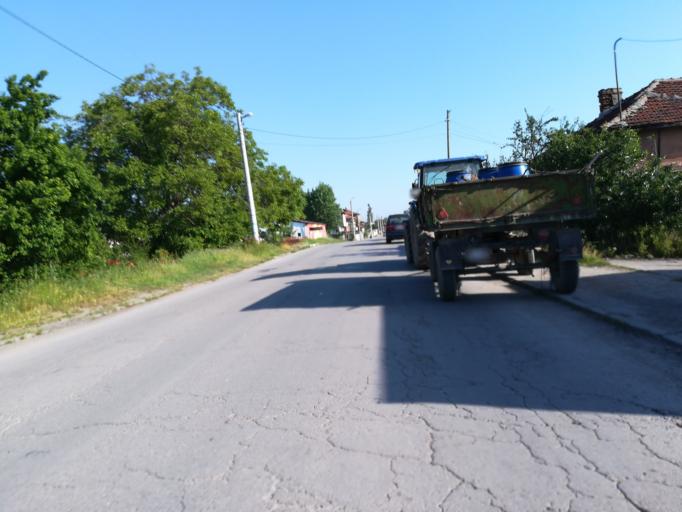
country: BG
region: Stara Zagora
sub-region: Obshtina Chirpan
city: Chirpan
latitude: 42.1049
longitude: 25.2277
